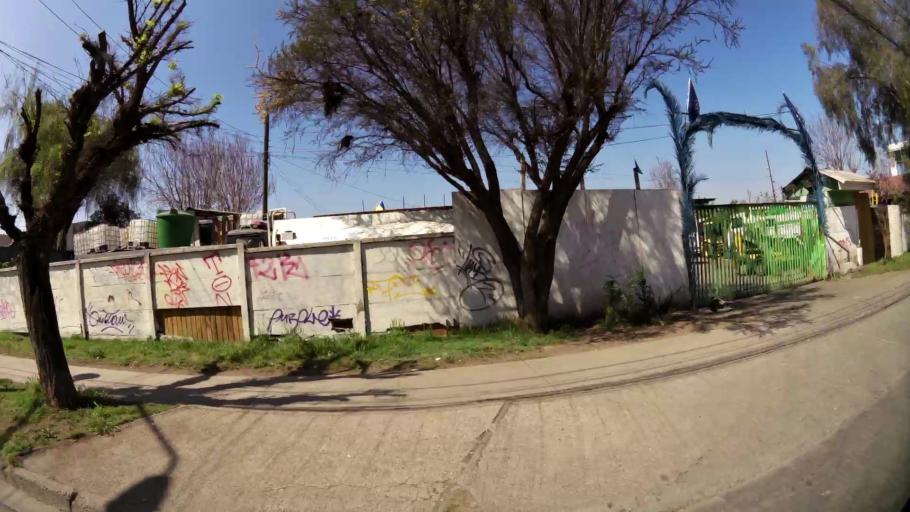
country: CL
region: Santiago Metropolitan
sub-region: Provincia de Santiago
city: Lo Prado
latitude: -33.3692
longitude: -70.7319
